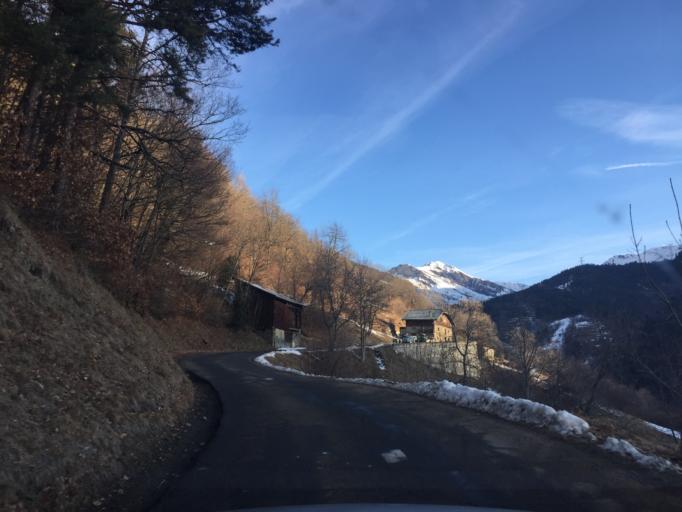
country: FR
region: Rhone-Alpes
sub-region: Departement de la Savoie
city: Aigueblanche
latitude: 45.5324
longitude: 6.4900
